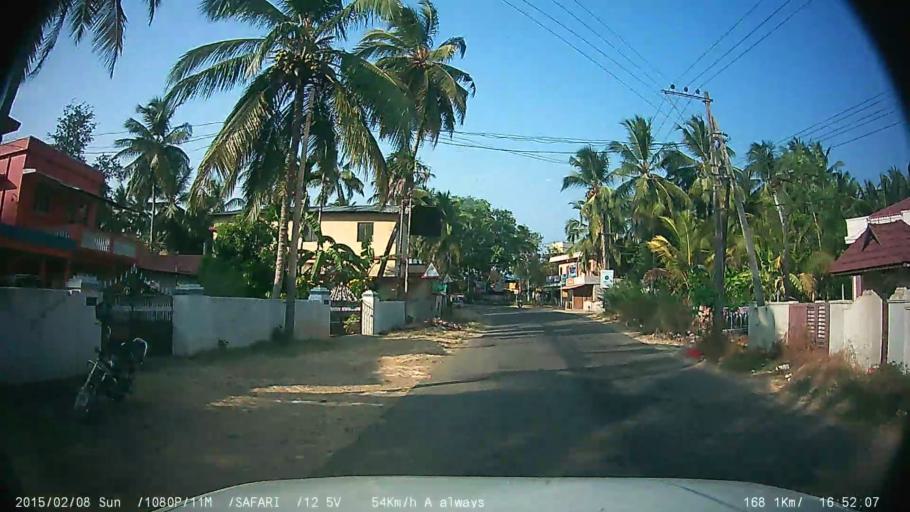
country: IN
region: Kerala
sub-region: Palakkad district
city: Palakkad
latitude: 10.7463
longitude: 76.6466
